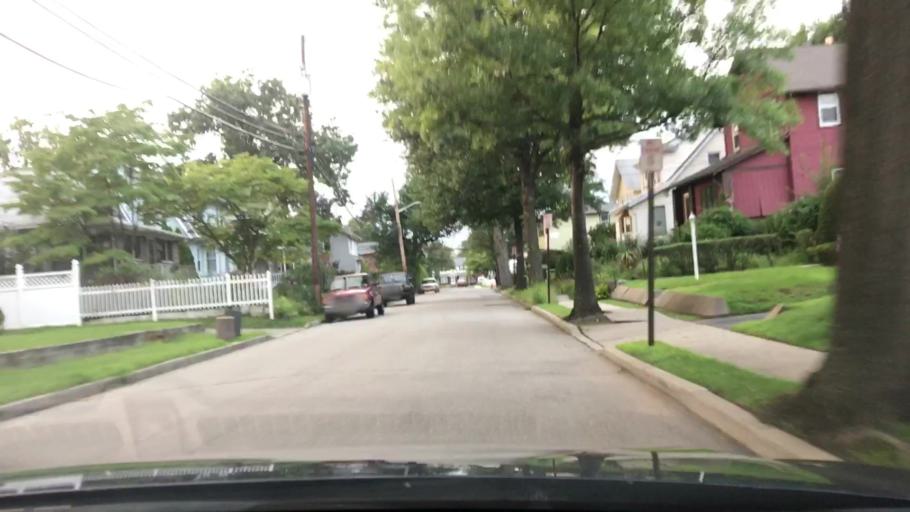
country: US
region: New Jersey
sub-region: Bergen County
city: Bergenfield
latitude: 40.9269
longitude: -73.9934
